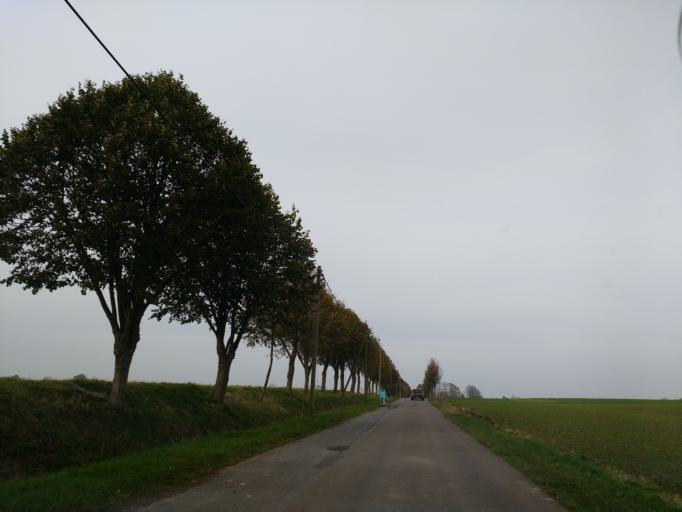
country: DE
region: Mecklenburg-Vorpommern
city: Ostseebad Boltenhagen
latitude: 53.9991
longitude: 11.1785
